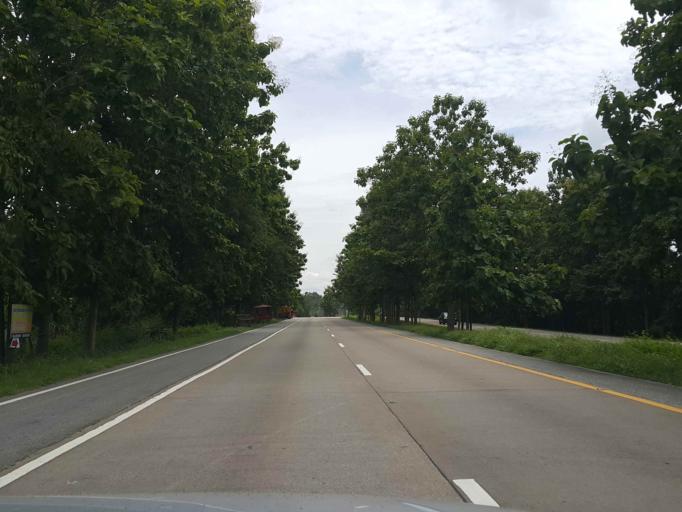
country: TH
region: Lamphun
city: Mae Tha
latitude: 18.4725
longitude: 99.1276
